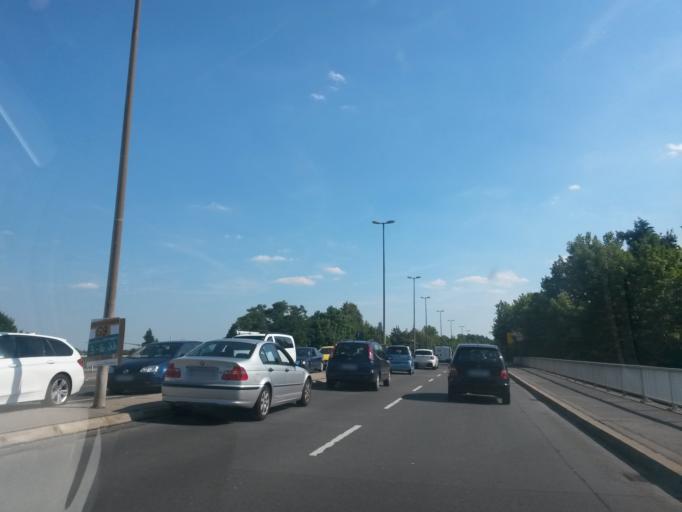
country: DE
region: Bavaria
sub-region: Regierungsbezirk Mittelfranken
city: Furth
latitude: 49.4559
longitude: 10.9757
